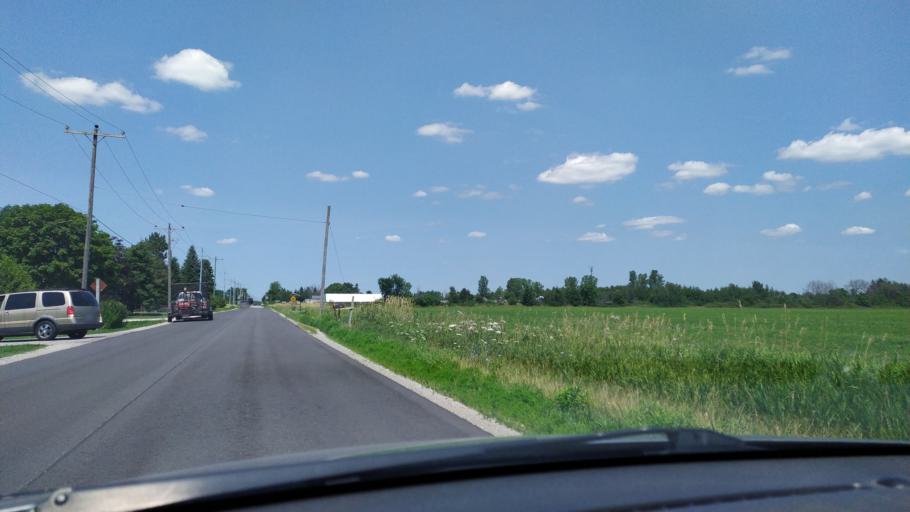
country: CA
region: Ontario
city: Stratford
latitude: 43.3635
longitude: -80.9377
